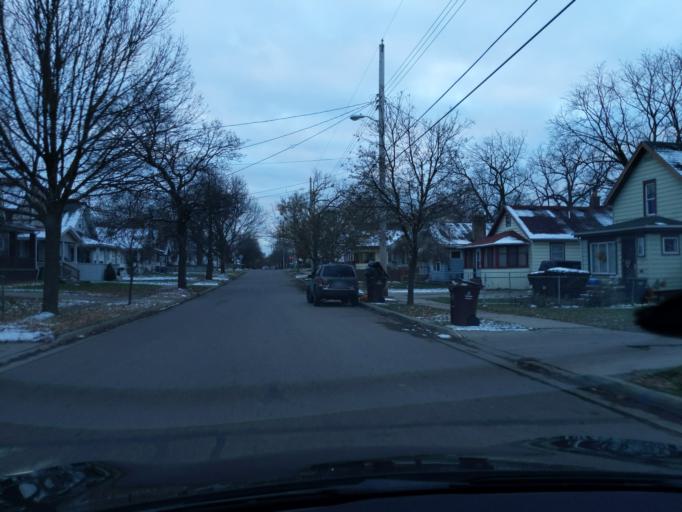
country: US
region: Michigan
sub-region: Ingham County
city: Lansing
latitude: 42.7527
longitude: -84.5372
